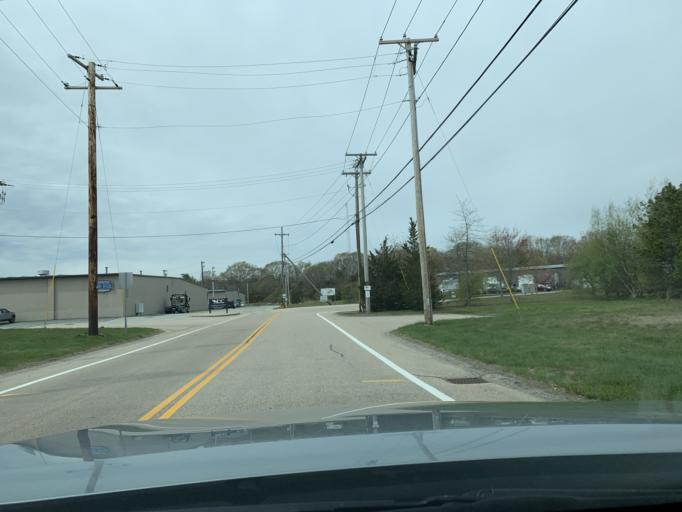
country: US
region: Rhode Island
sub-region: Washington County
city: North Kingstown
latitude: 41.6055
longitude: -71.4762
